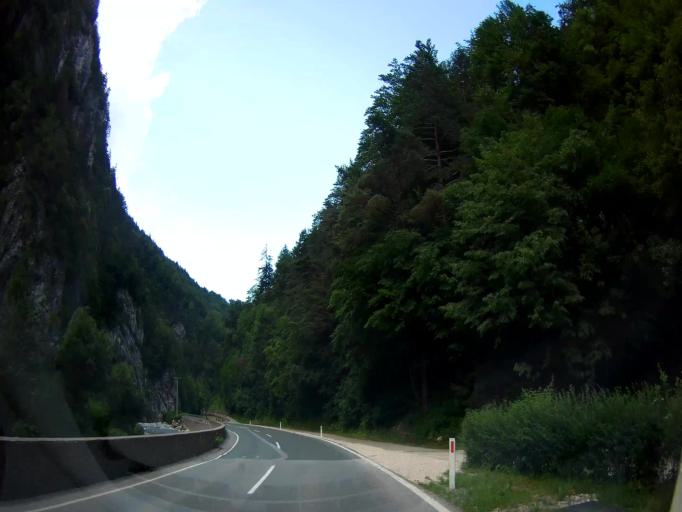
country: AT
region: Carinthia
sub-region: Politischer Bezirk Volkermarkt
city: Bad Eisenkappel
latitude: 46.4967
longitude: 14.5837
